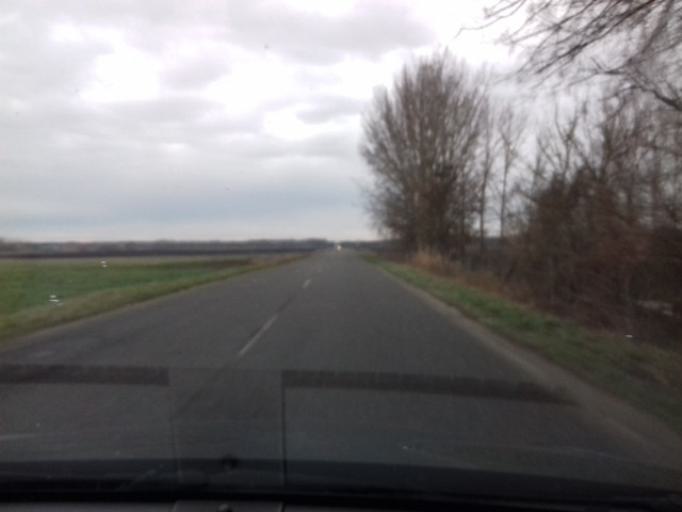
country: HU
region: Szabolcs-Szatmar-Bereg
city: Nyirbogdany
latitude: 48.0599
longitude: 21.8597
